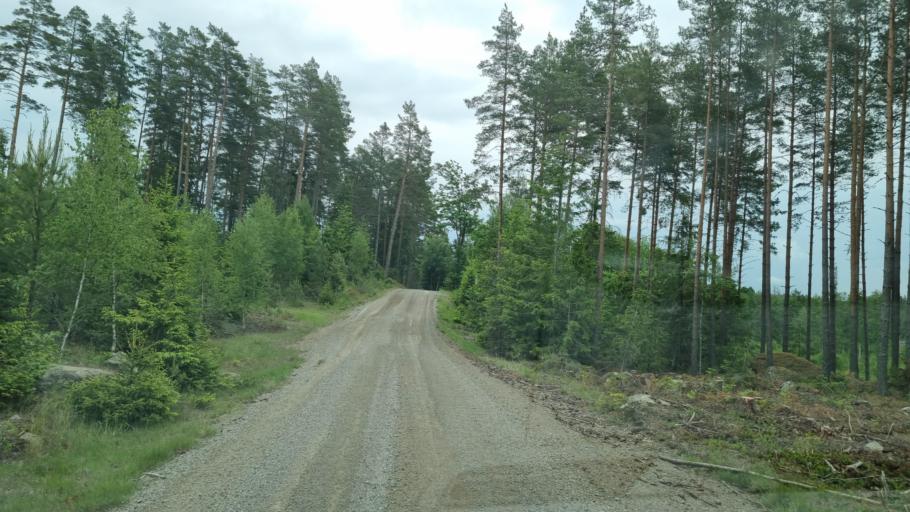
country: SE
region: OEstergoetland
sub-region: Atvidabergs Kommun
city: Atvidaberg
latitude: 58.2579
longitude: 16.0596
